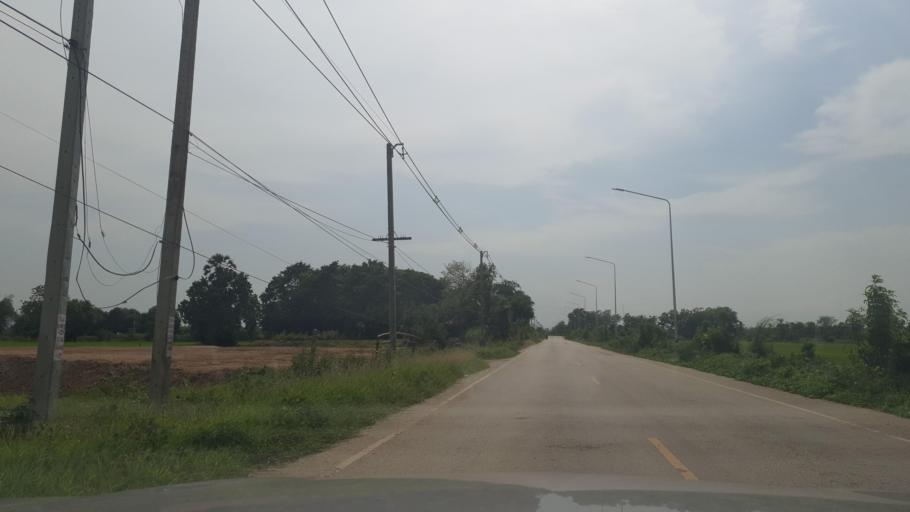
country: TH
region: Sukhothai
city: Si Samrong
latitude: 17.1395
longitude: 99.8440
